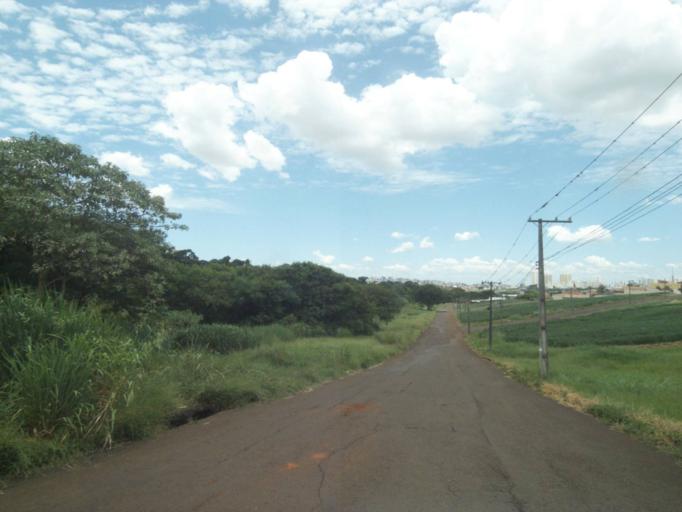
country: BR
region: Parana
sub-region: Londrina
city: Londrina
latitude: -23.3186
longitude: -51.2092
